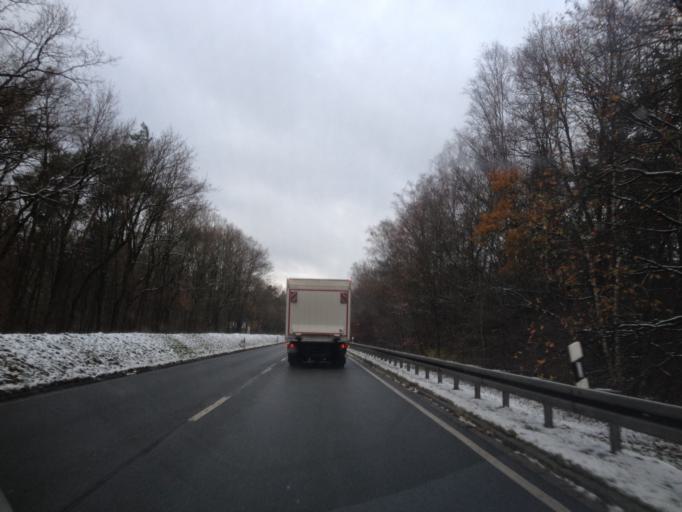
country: DE
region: Bavaria
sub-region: Regierungsbezirk Mittelfranken
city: Schwaig
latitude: 49.4739
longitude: 11.1528
